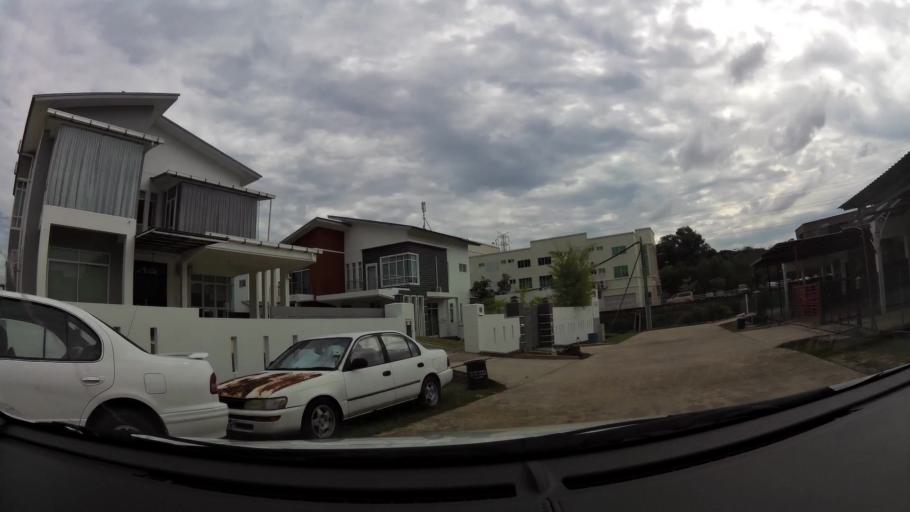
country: BN
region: Brunei and Muara
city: Bandar Seri Begawan
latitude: 4.8871
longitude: 114.8988
